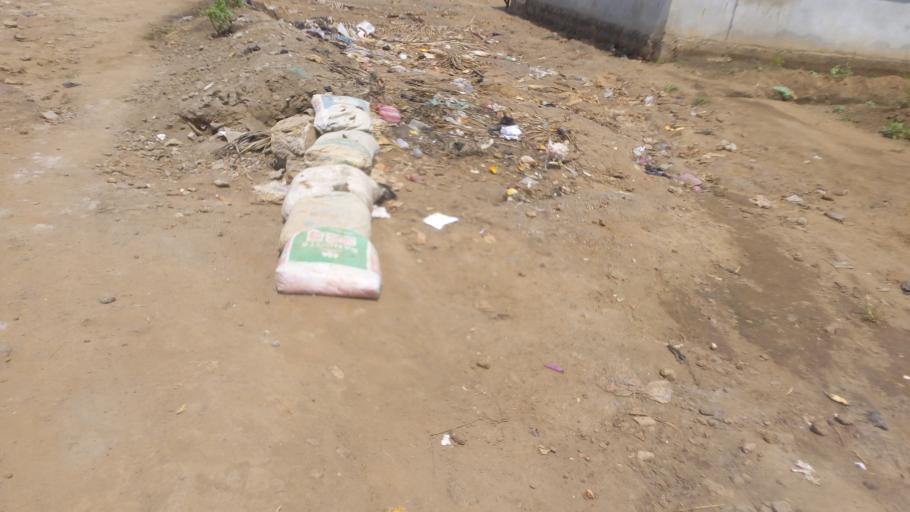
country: SL
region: Western Area
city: Waterloo
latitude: 8.3272
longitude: -13.0772
